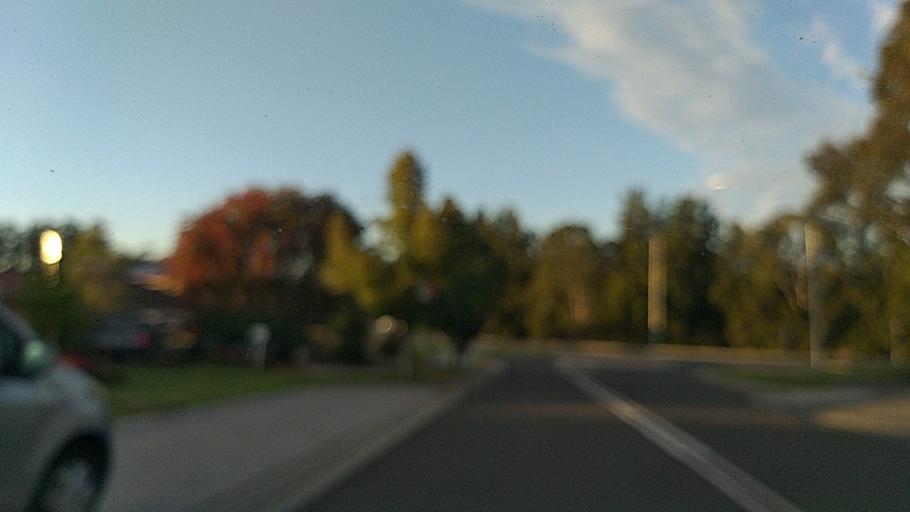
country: AU
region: New South Wales
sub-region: Wollongong
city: Dapto
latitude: -34.4952
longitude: 150.7777
